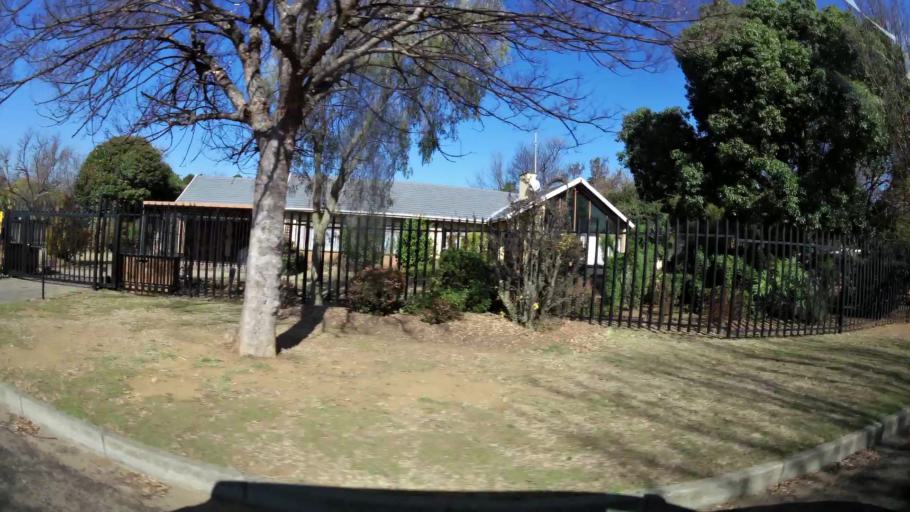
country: ZA
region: Gauteng
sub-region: Ekurhuleni Metropolitan Municipality
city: Benoni
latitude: -26.1380
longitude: 28.3434
